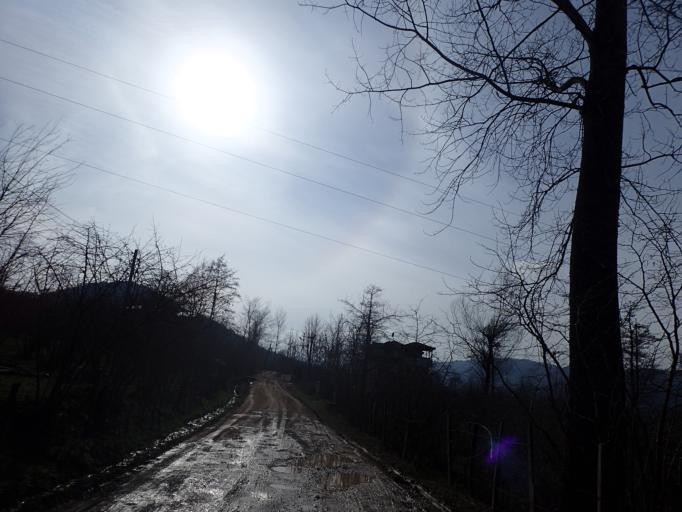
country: TR
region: Ordu
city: Camas
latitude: 40.9372
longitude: 37.5131
